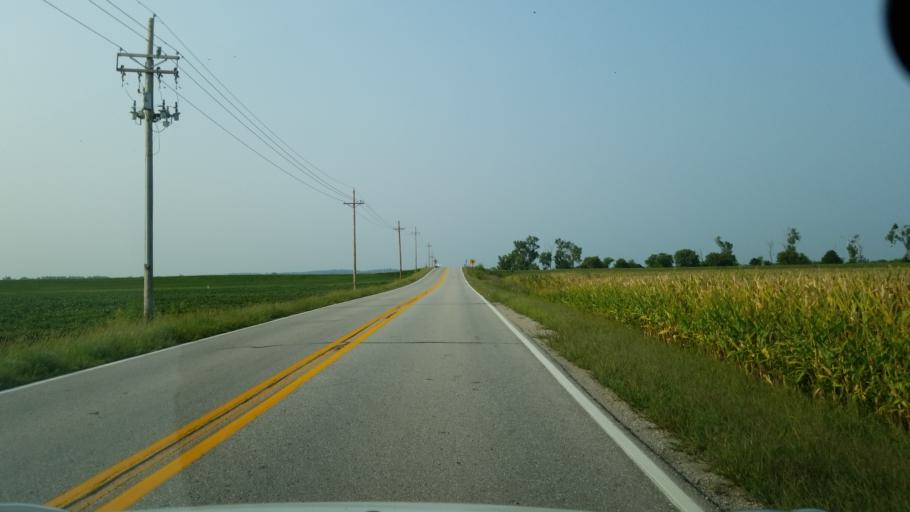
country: US
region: Nebraska
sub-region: Sarpy County
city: Offutt Air Force Base
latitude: 41.0796
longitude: -95.8898
